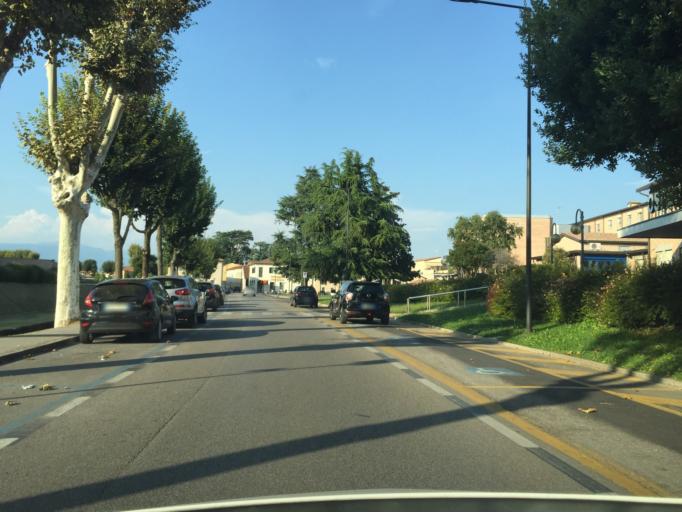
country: IT
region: Veneto
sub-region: Provincia di Padova
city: Cittadella
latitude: 45.6472
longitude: 11.7866
